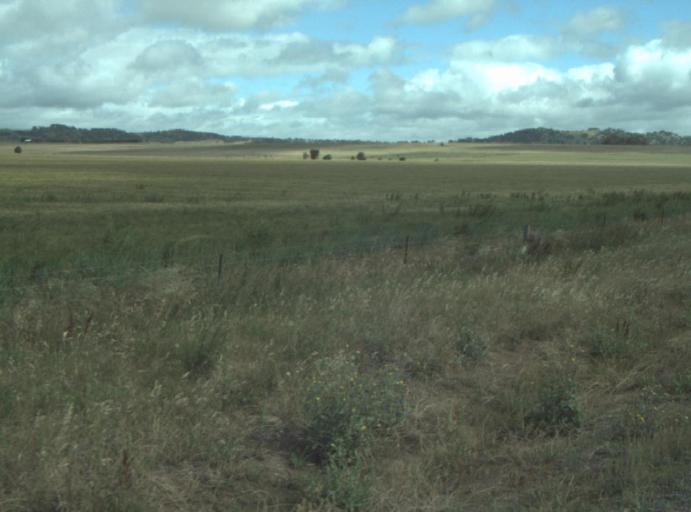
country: AU
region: Victoria
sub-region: Greater Geelong
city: Lara
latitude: -37.9054
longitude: 144.3166
